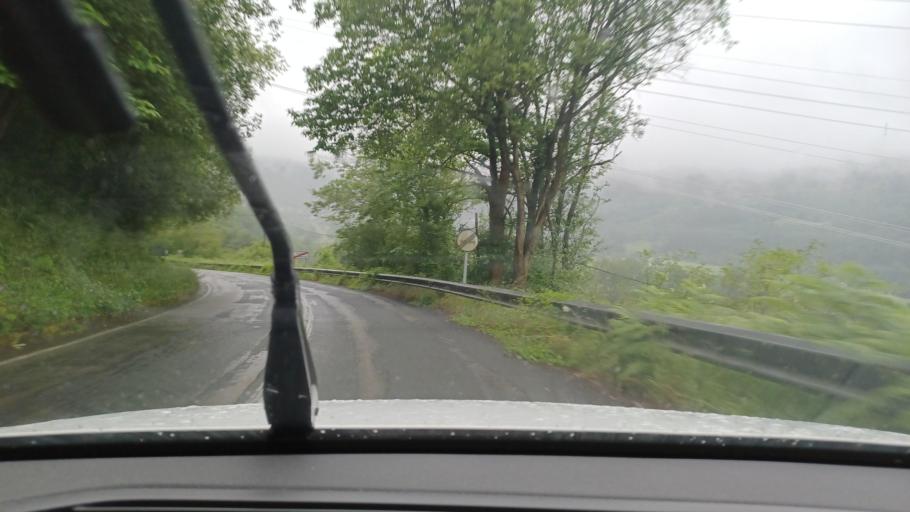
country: ES
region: Asturias
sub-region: Province of Asturias
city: Castandiello
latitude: 43.3093
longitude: -5.8926
